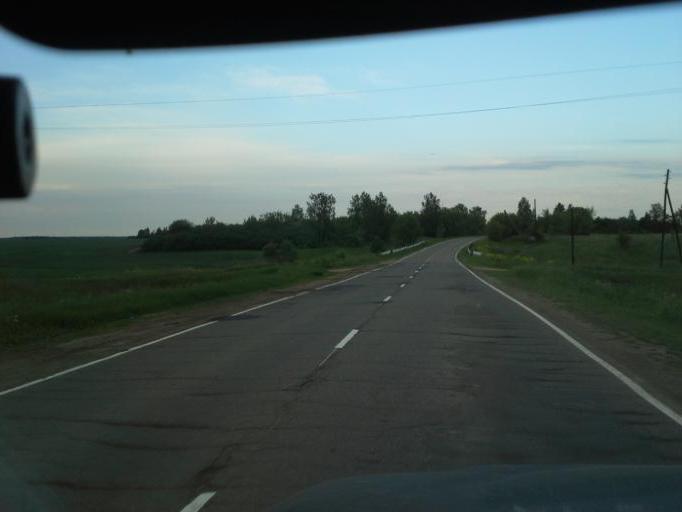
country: RU
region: Ivanovo
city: Gavrilov Posad
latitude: 56.5487
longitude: 40.1774
